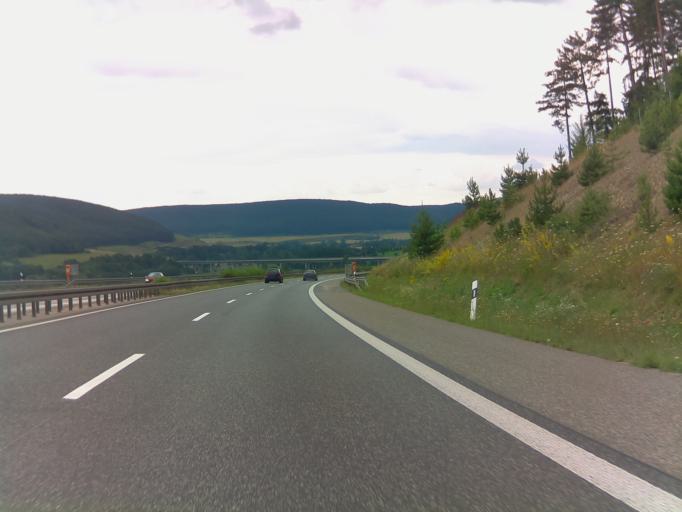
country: DE
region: Thuringia
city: Ellingshausen
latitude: 50.5680
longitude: 10.4788
